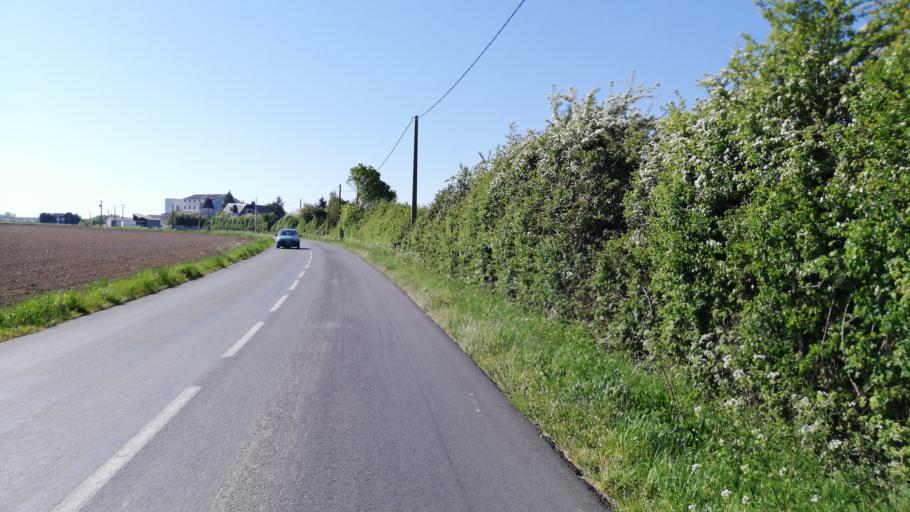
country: FR
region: Pays de la Loire
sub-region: Departement de la Vendee
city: Maillezais
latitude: 46.3282
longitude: -0.7437
